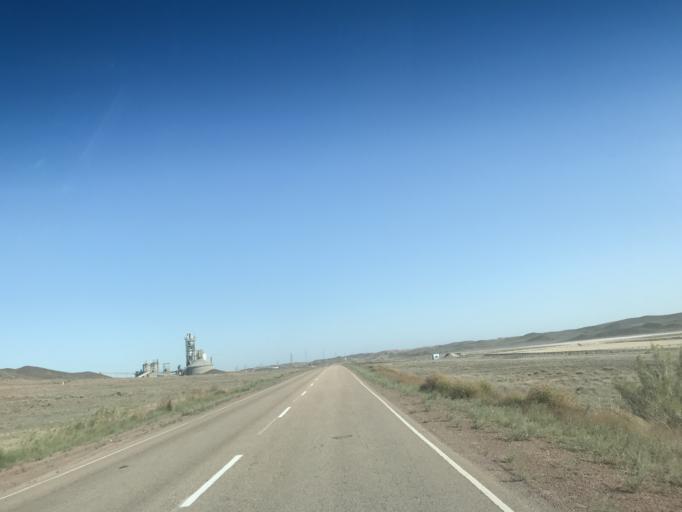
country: KZ
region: Zhambyl
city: Mynaral
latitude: 45.3978
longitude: 73.6409
